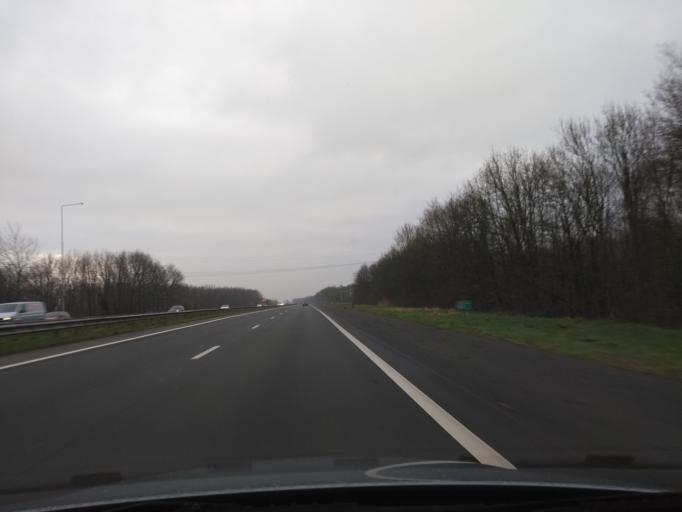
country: NL
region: Overijssel
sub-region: Gemeente Borne
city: Borne
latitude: 52.2651
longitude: 6.7507
